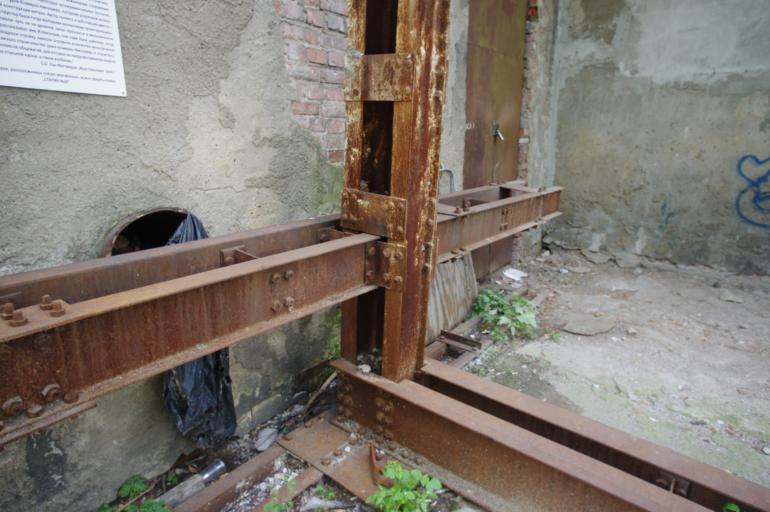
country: RU
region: Moscow
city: Novyye Cheremushki
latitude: 55.7106
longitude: 37.5967
